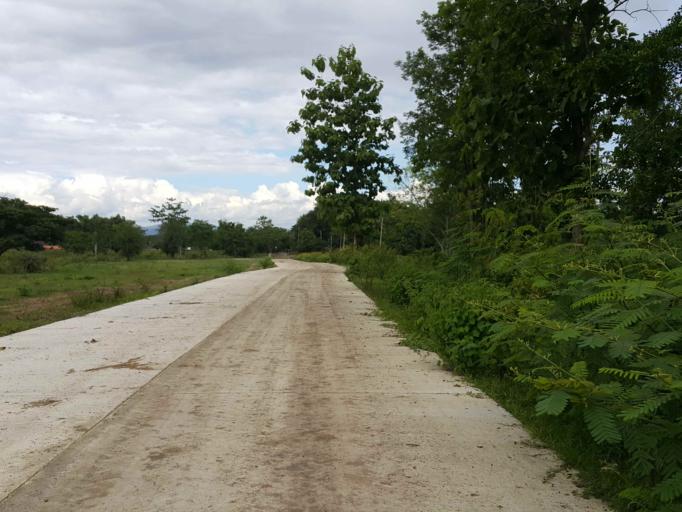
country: TH
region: Chiang Mai
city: San Sai
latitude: 18.9435
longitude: 98.9160
